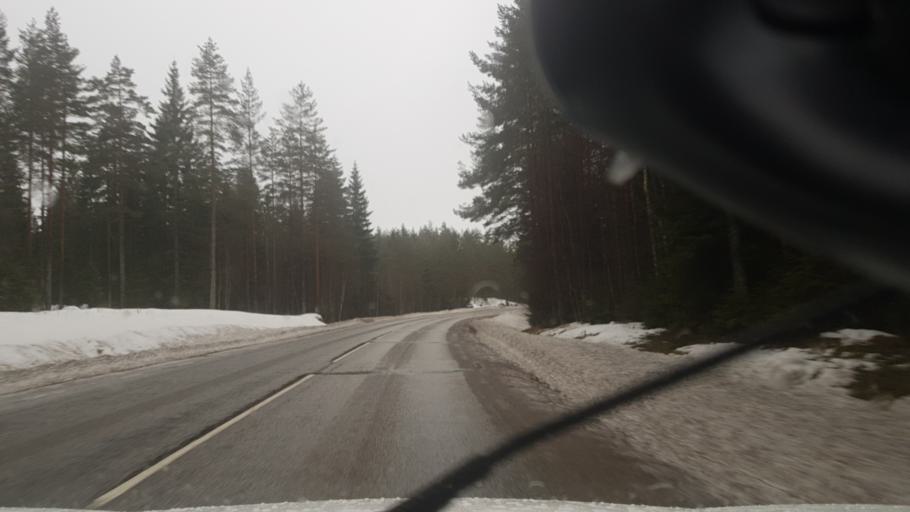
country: SE
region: Vaermland
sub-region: Eda Kommun
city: Amotfors
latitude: 59.5888
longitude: 12.2965
